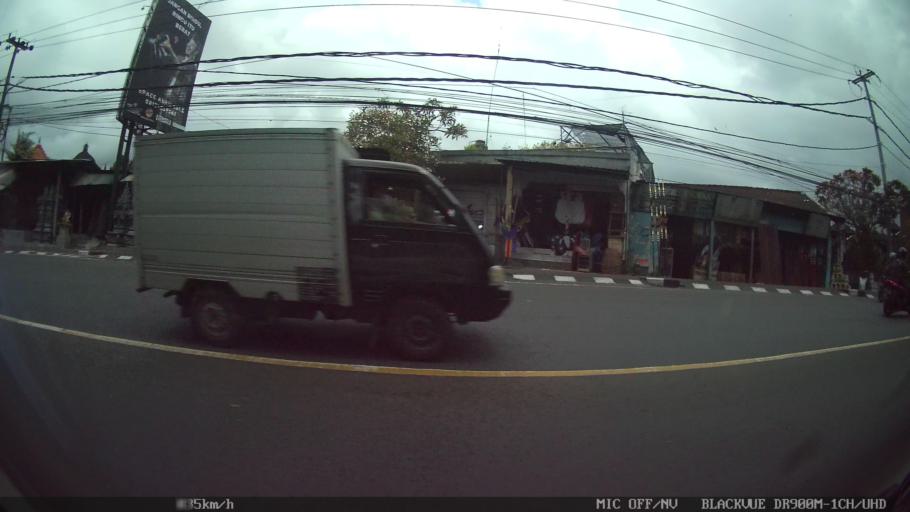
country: ID
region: Bali
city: Banjar Jumbayah
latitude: -8.5662
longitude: 115.1736
